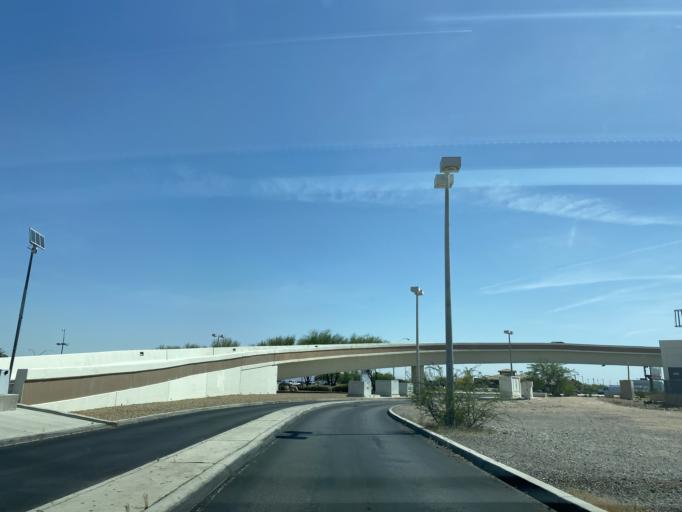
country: US
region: Nevada
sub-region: Clark County
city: Paradise
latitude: 36.0663
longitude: -115.1737
